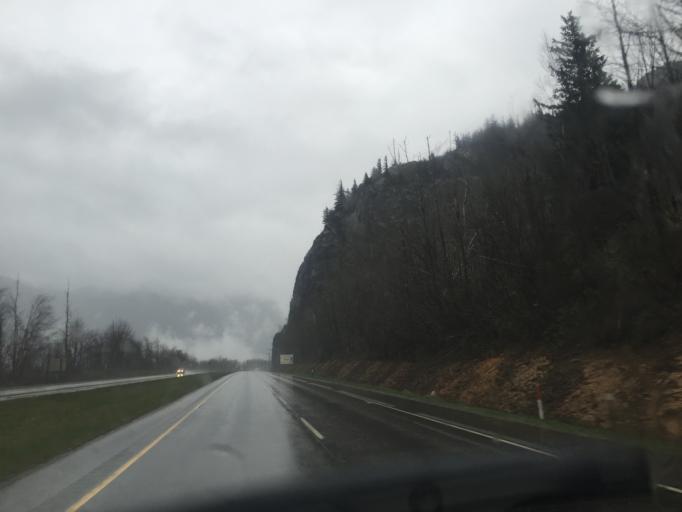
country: CA
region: British Columbia
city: Hope
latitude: 49.3590
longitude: -121.5714
